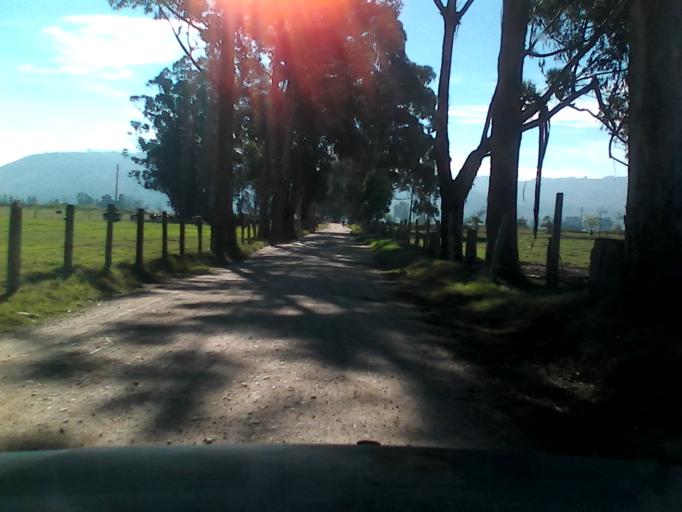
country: CO
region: Boyaca
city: Duitama
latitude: 5.7850
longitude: -73.0450
